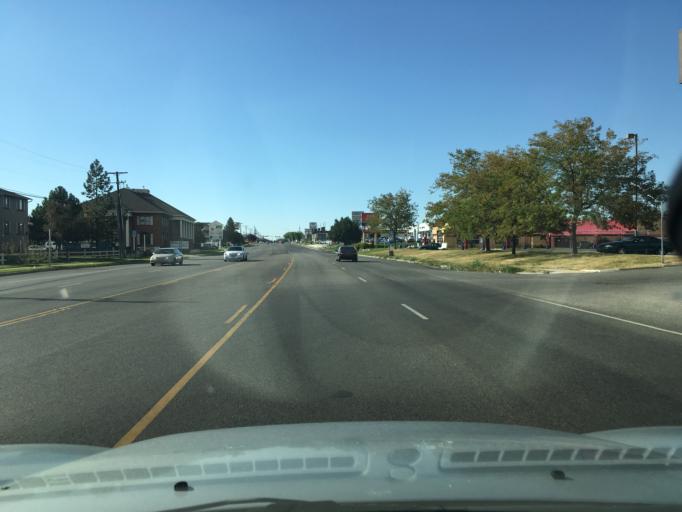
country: US
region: Utah
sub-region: Davis County
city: Layton
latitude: 41.0763
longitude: -111.9827
